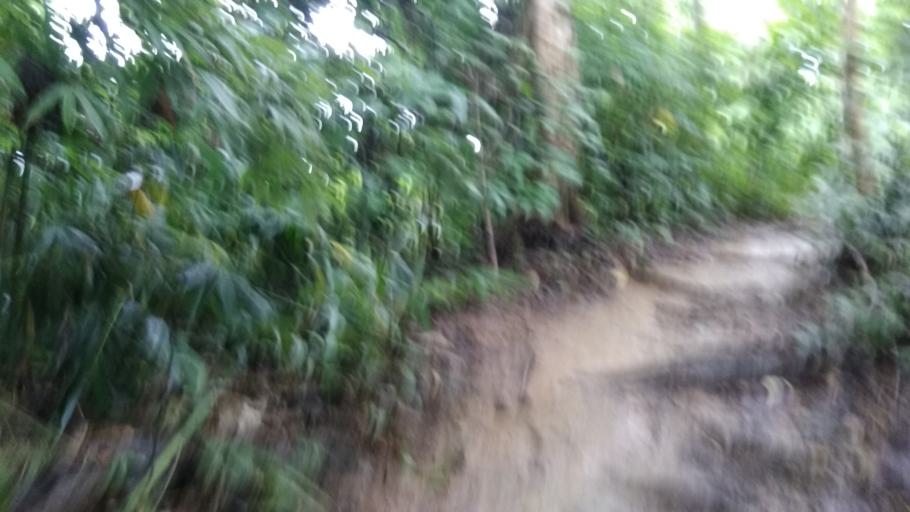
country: IN
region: Tripura
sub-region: Dhalai
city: Kamalpur
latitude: 24.1709
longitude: 91.8943
